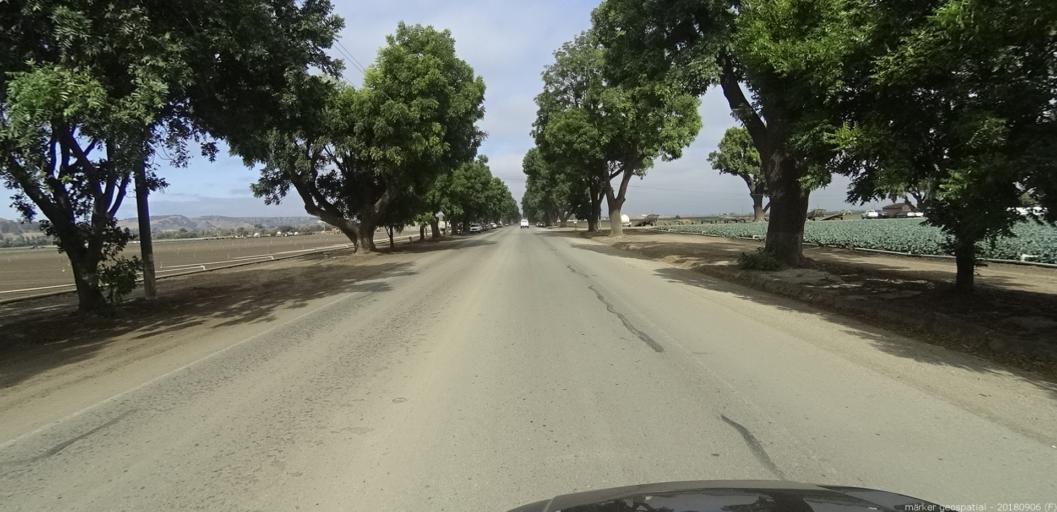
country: US
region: California
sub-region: Monterey County
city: Salinas
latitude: 36.6259
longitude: -121.6564
